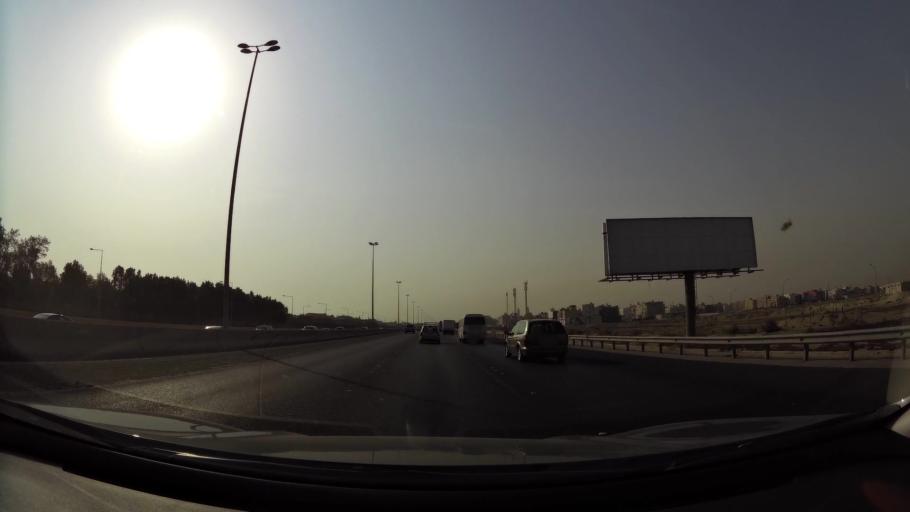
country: KW
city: Al Funaytis
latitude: 29.2427
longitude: 48.0937
